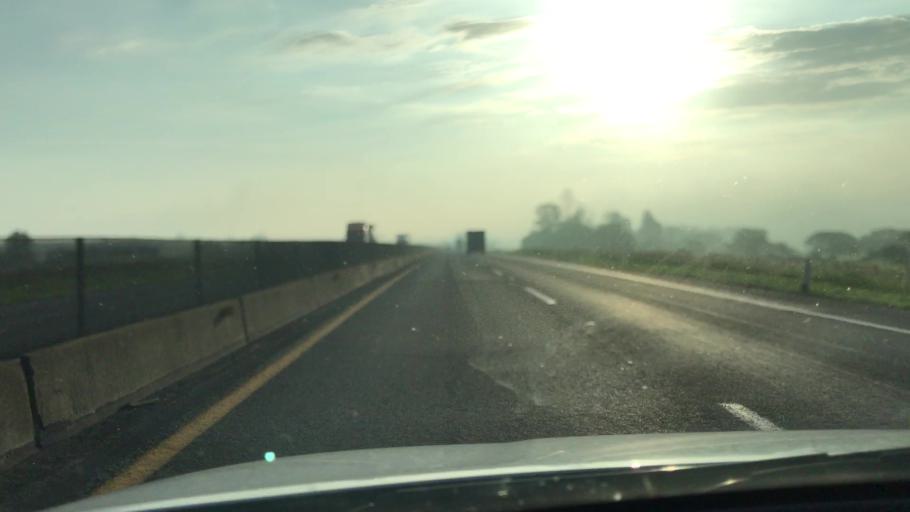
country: MX
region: Jalisco
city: Tepatitlan de Morelos
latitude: 20.8746
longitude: -102.7436
